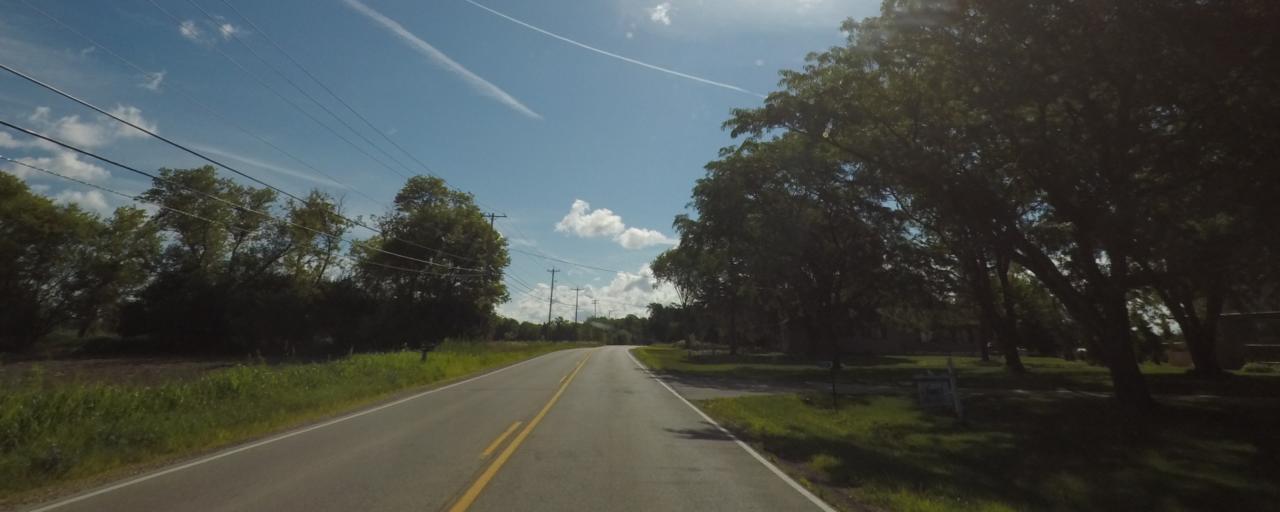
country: US
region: Wisconsin
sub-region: Waukesha County
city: Oconomowoc
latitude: 43.0848
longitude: -88.5165
